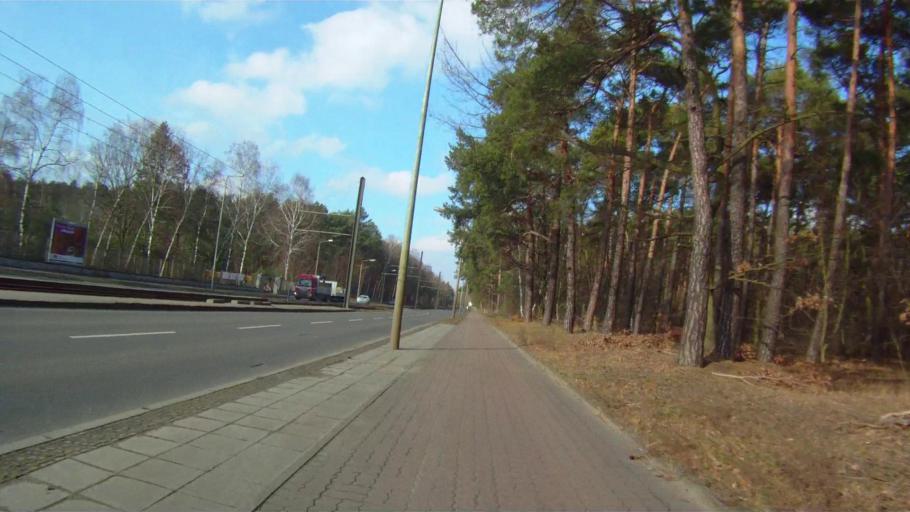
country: DE
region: Berlin
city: Schmockwitz
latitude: 52.3817
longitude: 13.6401
